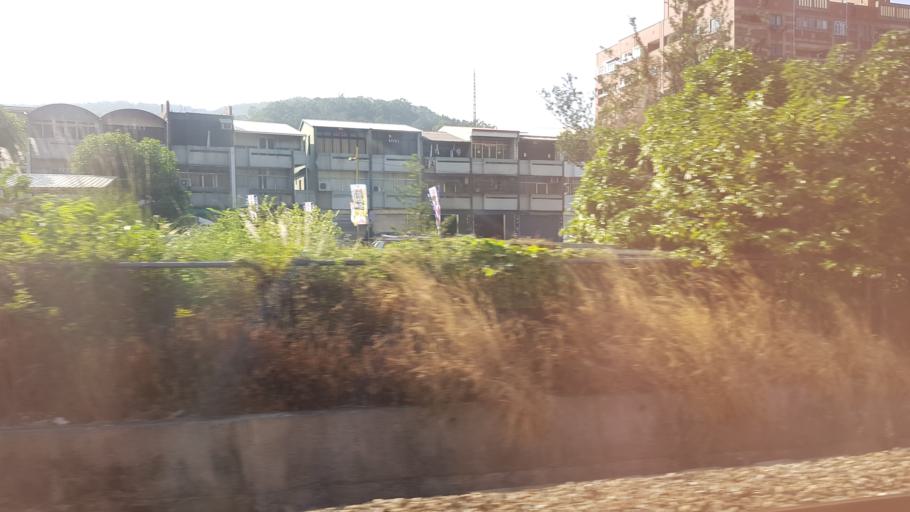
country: TW
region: Taiwan
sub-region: Miaoli
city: Miaoli
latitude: 24.4187
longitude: 120.7743
